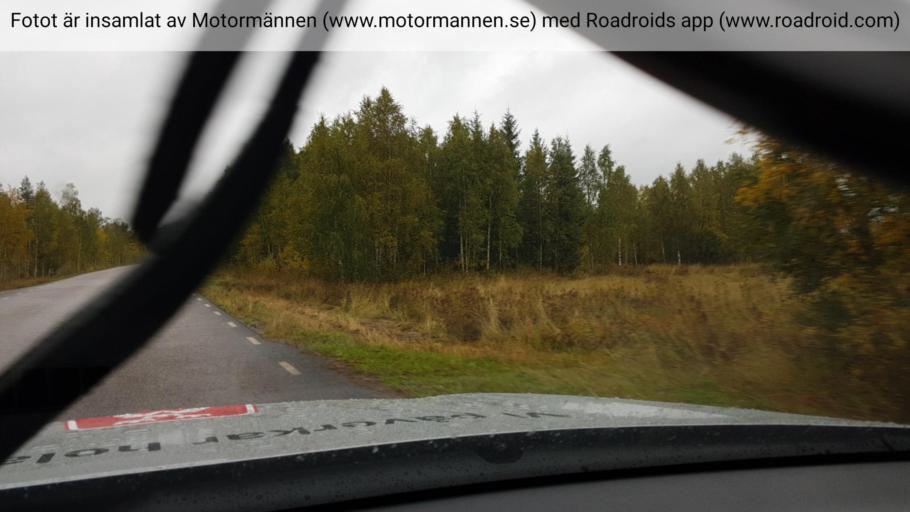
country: SE
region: Norrbotten
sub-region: Lulea Kommun
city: Gammelstad
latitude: 65.7327
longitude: 22.1223
